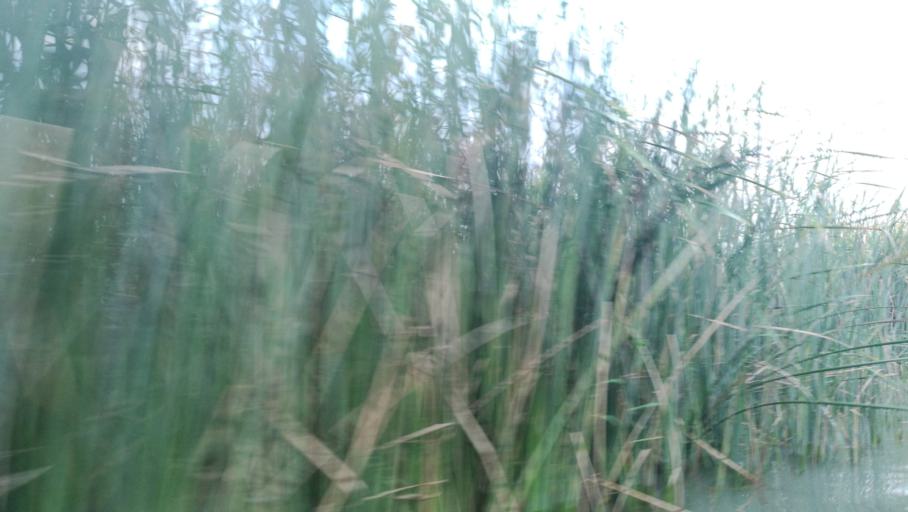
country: IQ
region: Dhi Qar
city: Al Jabayish
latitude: 30.9832
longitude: 47.0428
